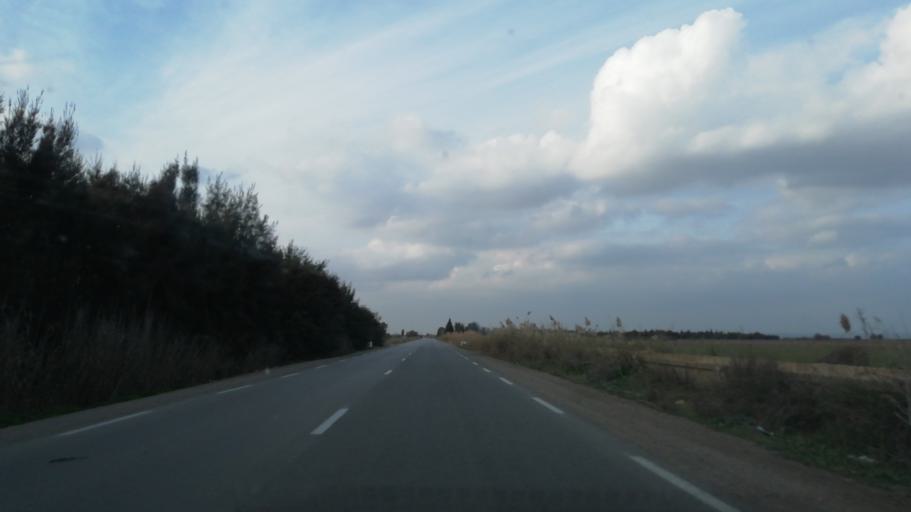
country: DZ
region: Mascara
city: Sig
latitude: 35.6443
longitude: 0.0284
